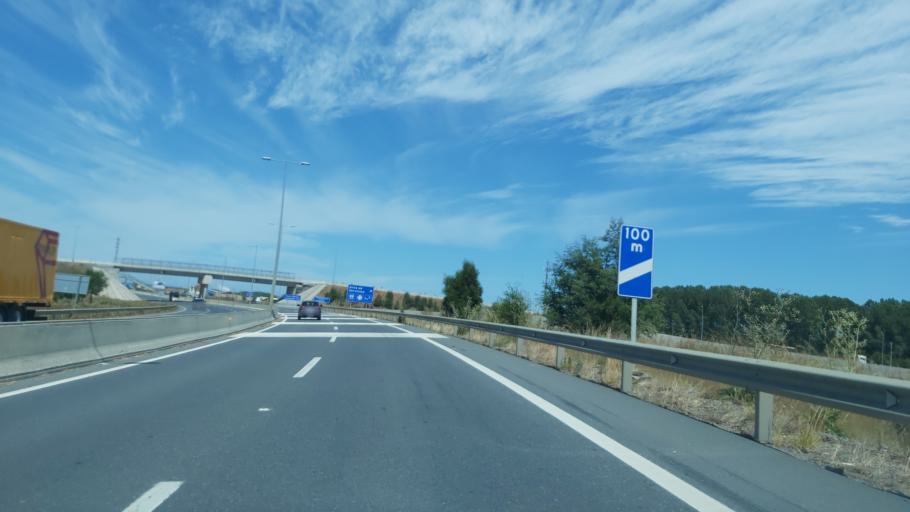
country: CL
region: Biobio
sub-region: Provincia de Concepcion
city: Lota
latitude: -37.1851
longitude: -73.1946
